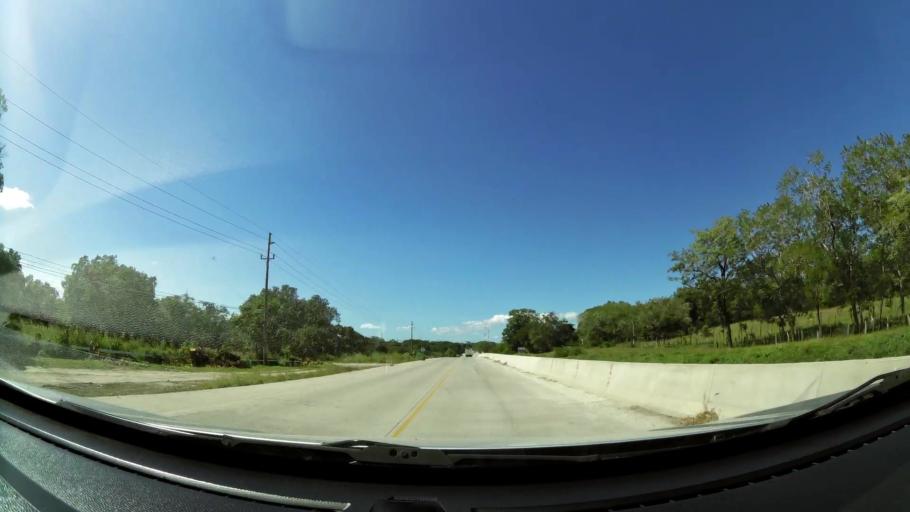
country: CR
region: Guanacaste
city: Liberia
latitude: 10.5631
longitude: -85.3845
